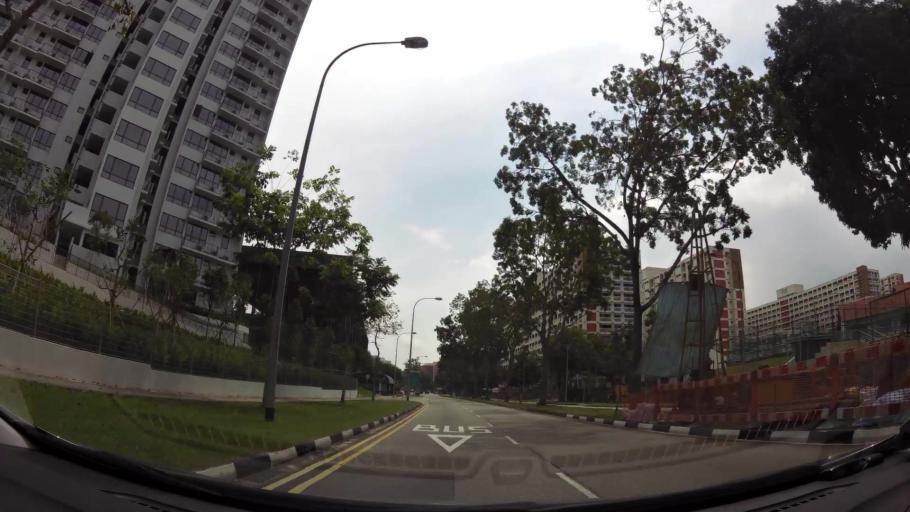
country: MY
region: Johor
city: Kampung Pasir Gudang Baru
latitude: 1.3810
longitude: 103.9400
